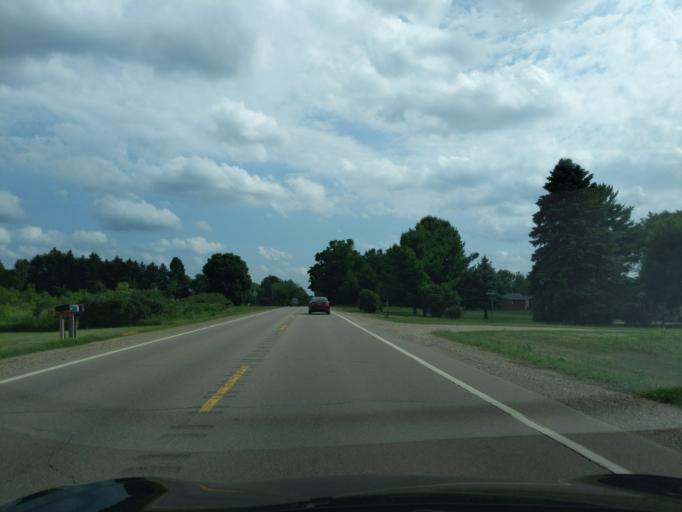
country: US
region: Michigan
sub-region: Eaton County
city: Eaton Rapids
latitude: 42.4721
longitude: -84.6597
